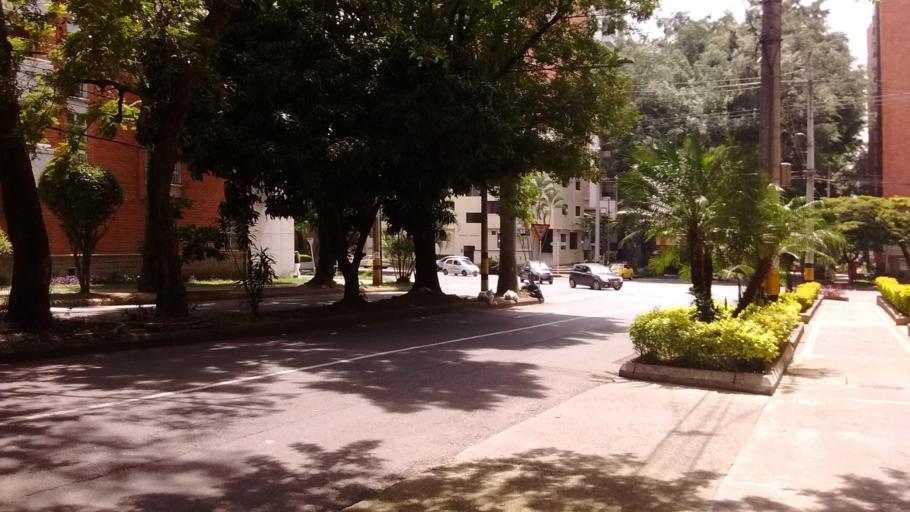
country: CO
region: Antioquia
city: Medellin
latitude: 6.2434
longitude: -75.5988
